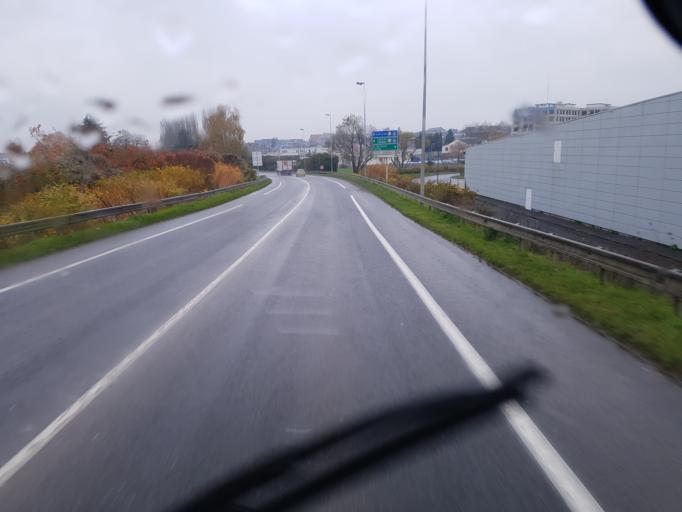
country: FR
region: Picardie
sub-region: Departement de l'Aisne
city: Saint-Quentin
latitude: 49.8388
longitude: 3.2840
